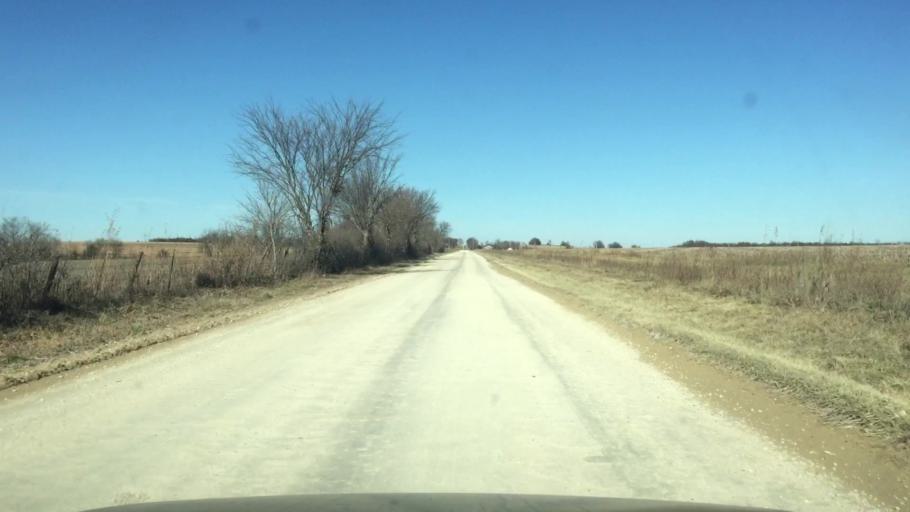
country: US
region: Kansas
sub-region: Allen County
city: Iola
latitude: 37.8685
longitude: -95.3911
